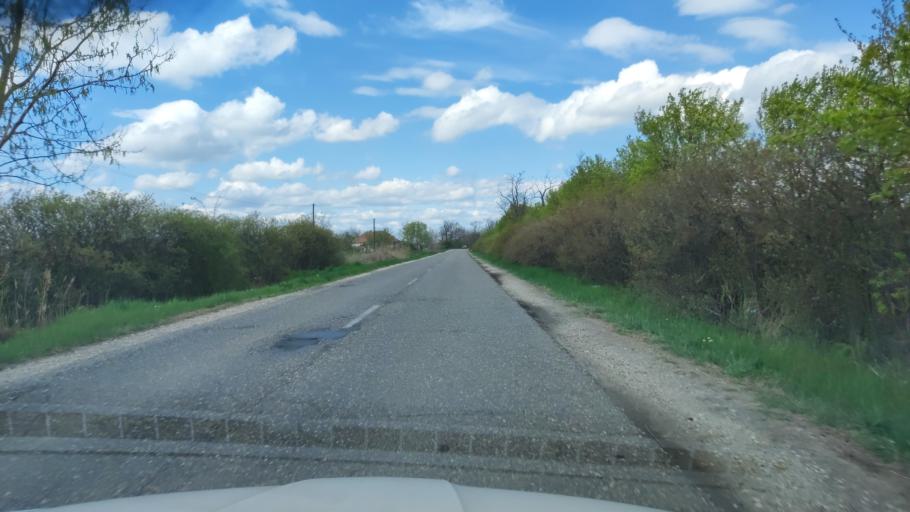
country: HU
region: Pest
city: Tortel
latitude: 47.1285
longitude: 19.9208
